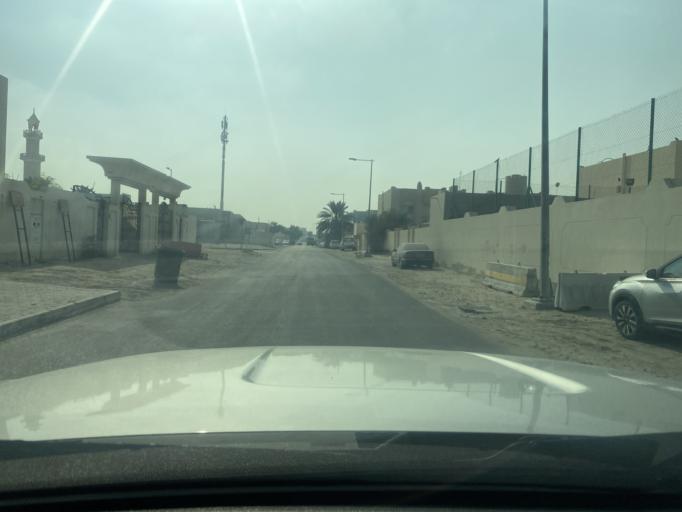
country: QA
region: Baladiyat ad Dawhah
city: Doha
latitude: 25.2380
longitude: 51.5685
